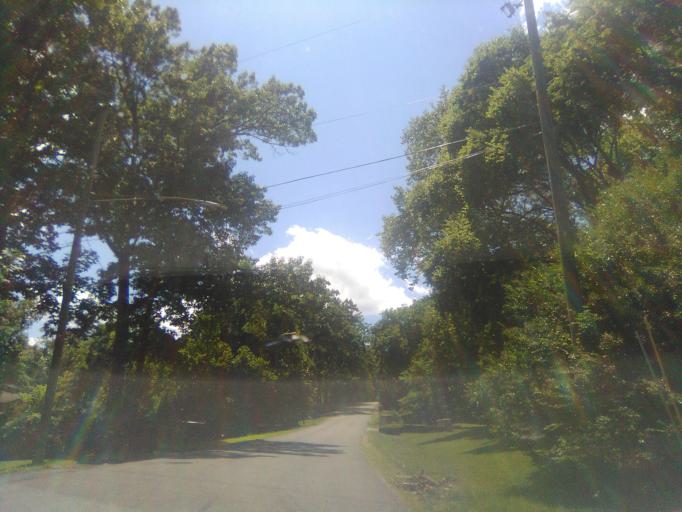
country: US
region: Tennessee
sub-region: Davidson County
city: Belle Meade
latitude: 36.1329
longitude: -86.8665
